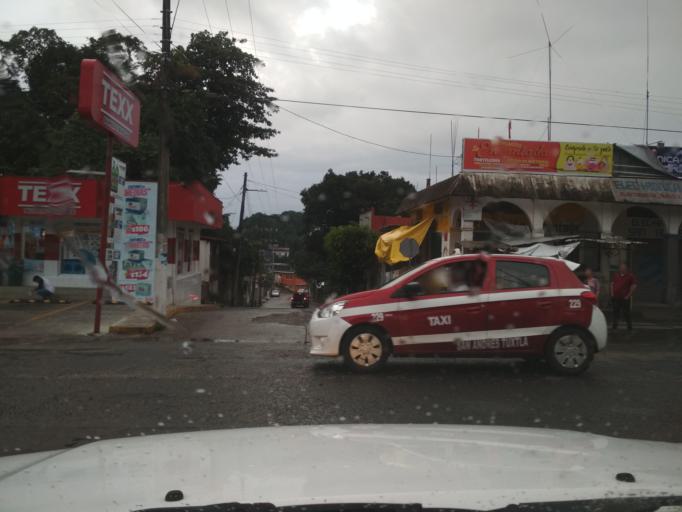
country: MX
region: Veracruz
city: San Andres Tuxtla
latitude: 18.4472
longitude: -95.2033
